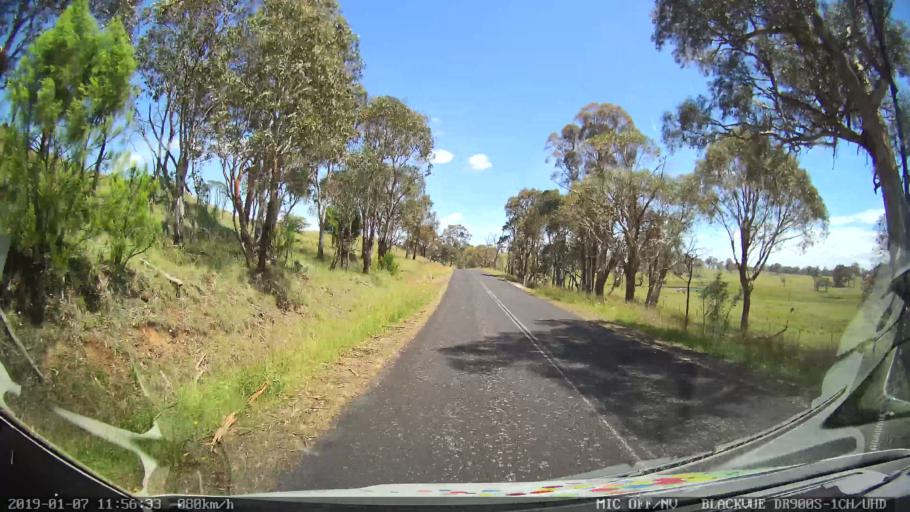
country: AU
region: New South Wales
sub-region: Guyra
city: Guyra
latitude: -30.2733
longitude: 151.6731
